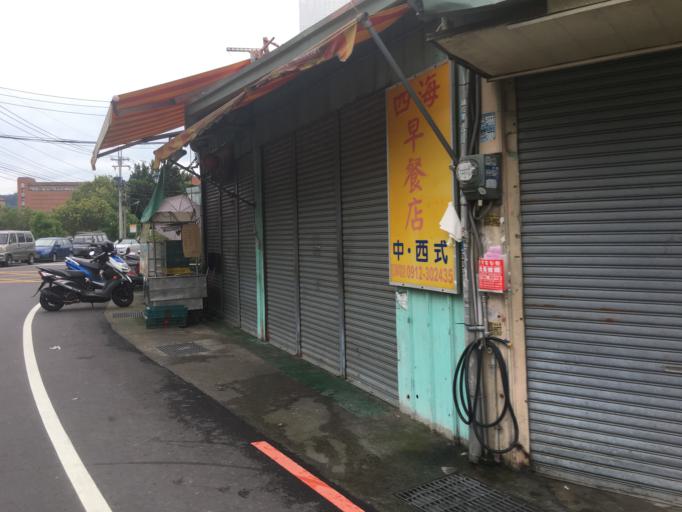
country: TW
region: Taiwan
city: Zhongxing New Village
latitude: 24.0499
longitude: 120.6862
